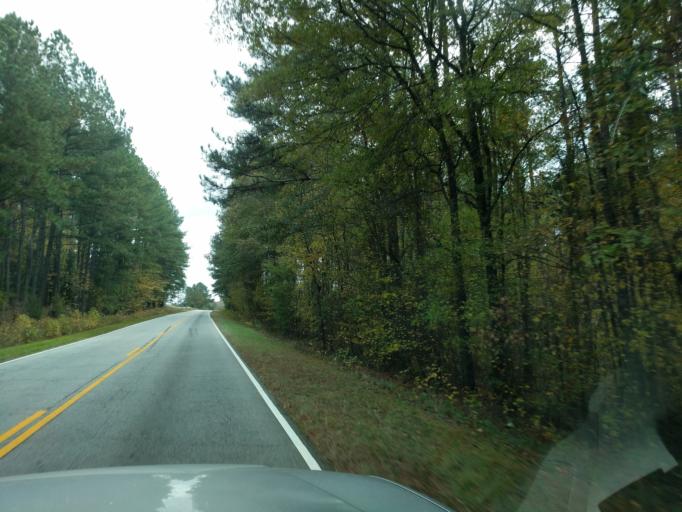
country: US
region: South Carolina
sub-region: Greenwood County
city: Ninety Six
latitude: 34.1668
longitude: -81.8577
